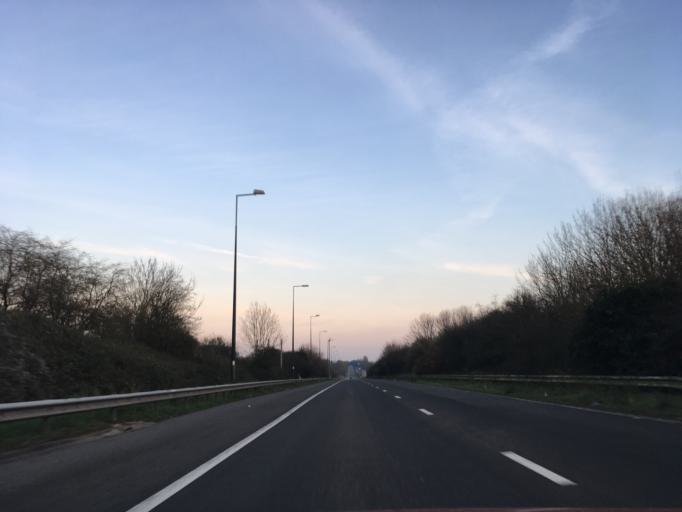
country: GB
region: Wales
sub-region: Monmouthshire
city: Rogiet
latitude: 51.5880
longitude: -2.8033
